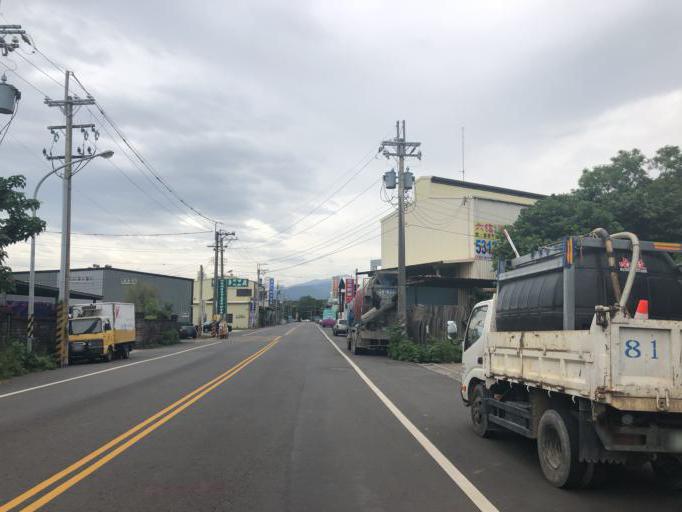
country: TW
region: Taiwan
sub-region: Hsinchu
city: Zhubei
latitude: 24.7278
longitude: 121.0965
